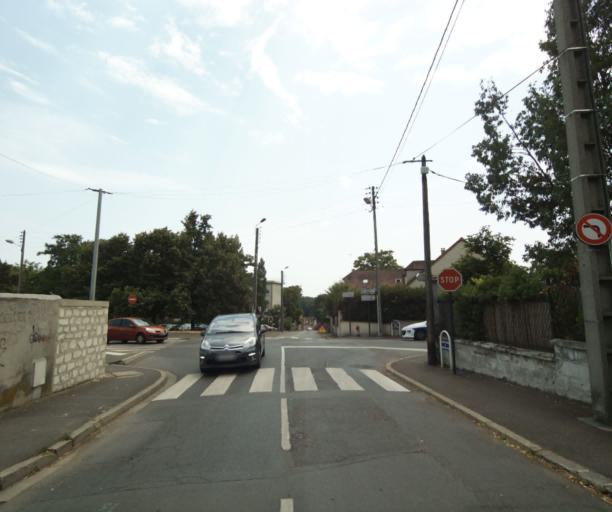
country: FR
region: Ile-de-France
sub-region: Departement des Yvelines
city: Conflans-Sainte-Honorine
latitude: 48.9928
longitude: 2.0874
